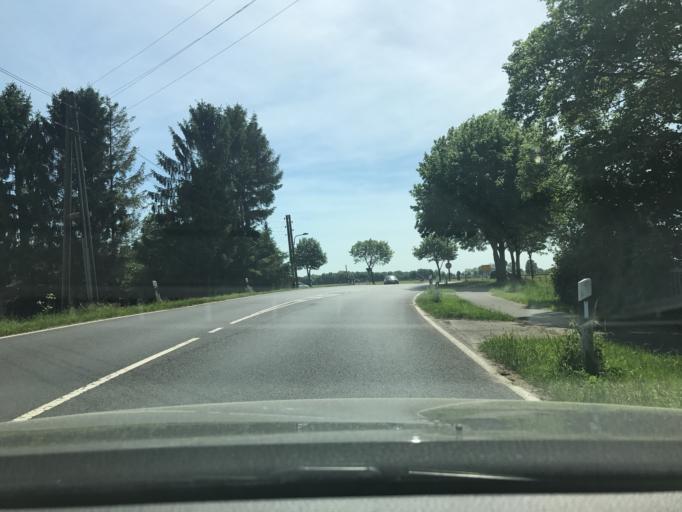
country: DE
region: North Rhine-Westphalia
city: Tonisvorst
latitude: 51.3406
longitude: 6.4650
